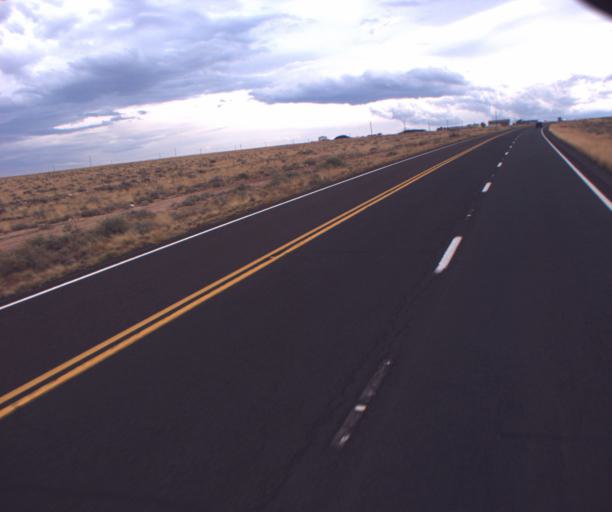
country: US
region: Arizona
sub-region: Coconino County
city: Tuba City
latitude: 35.7611
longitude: -111.4668
